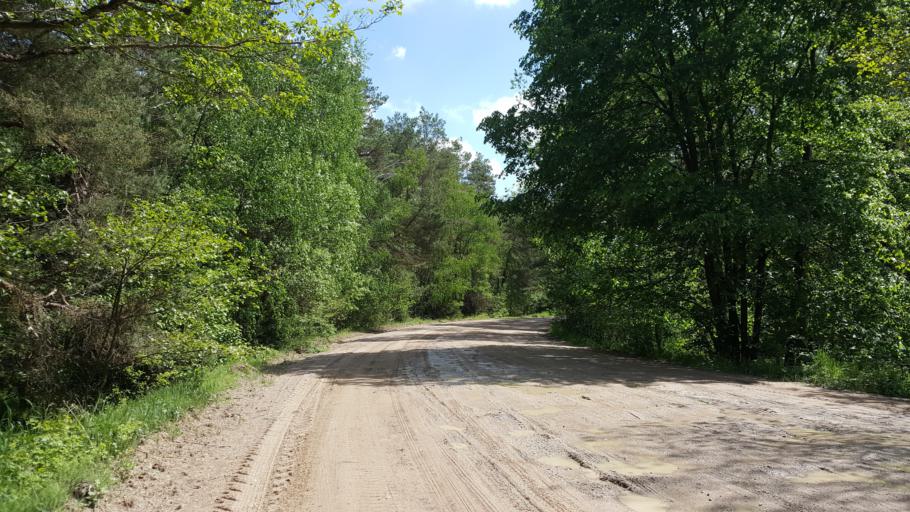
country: BY
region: Brest
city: Kamyanyets
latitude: 52.4225
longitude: 23.9494
